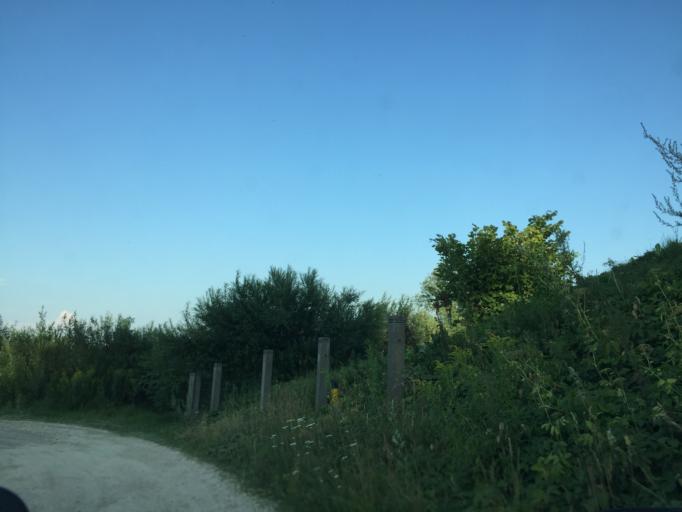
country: LV
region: Garkalne
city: Garkalne
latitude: 56.9785
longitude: 24.3805
